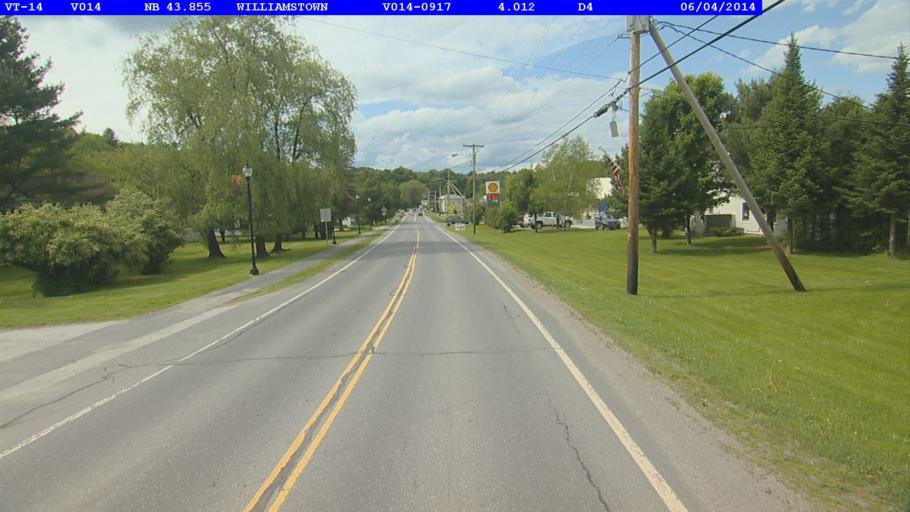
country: US
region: Vermont
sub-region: Orange County
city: Williamstown
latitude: 44.1156
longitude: -72.5397
